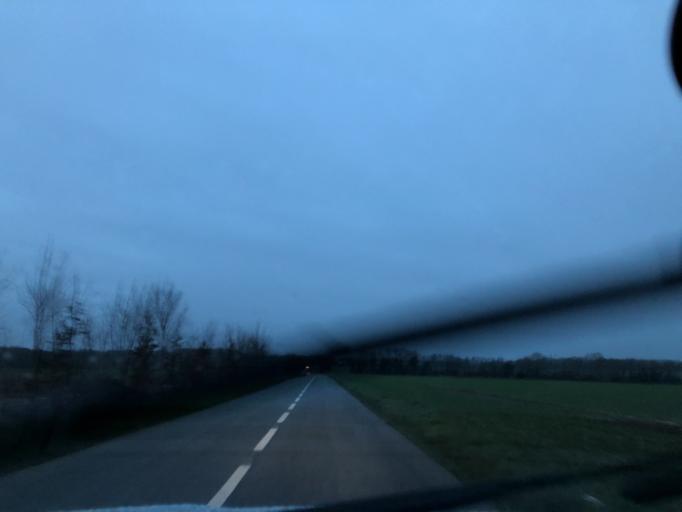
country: FR
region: Lower Normandy
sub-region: Departement du Calvados
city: Blainville-sur-Orne
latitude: 49.2353
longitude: -0.3097
